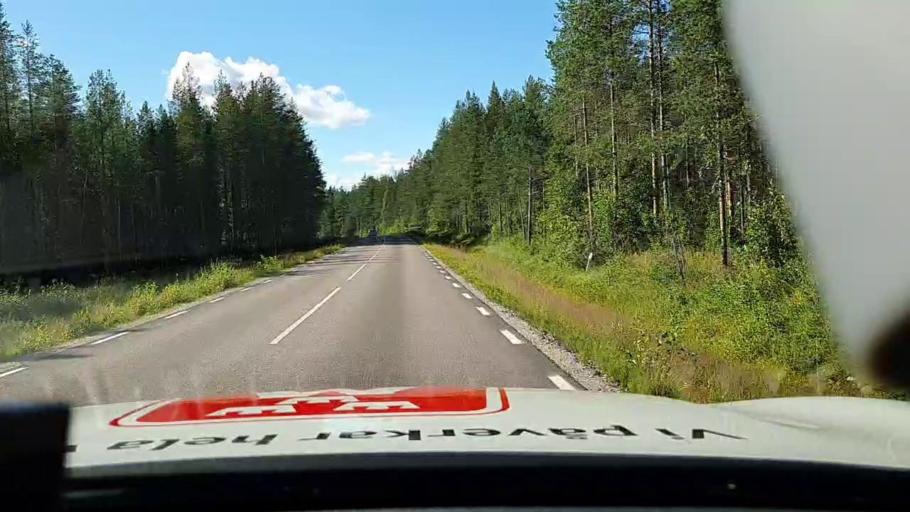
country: SE
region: Norrbotten
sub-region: Overkalix Kommun
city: OEverkalix
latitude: 66.2578
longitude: 22.8568
